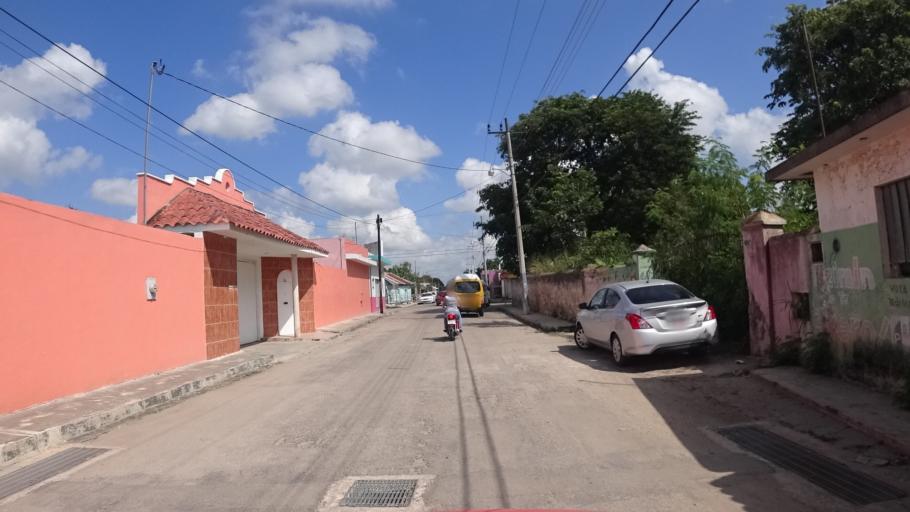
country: MX
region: Yucatan
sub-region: Tizimin
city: Tizimin
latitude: 21.1477
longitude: -88.1531
